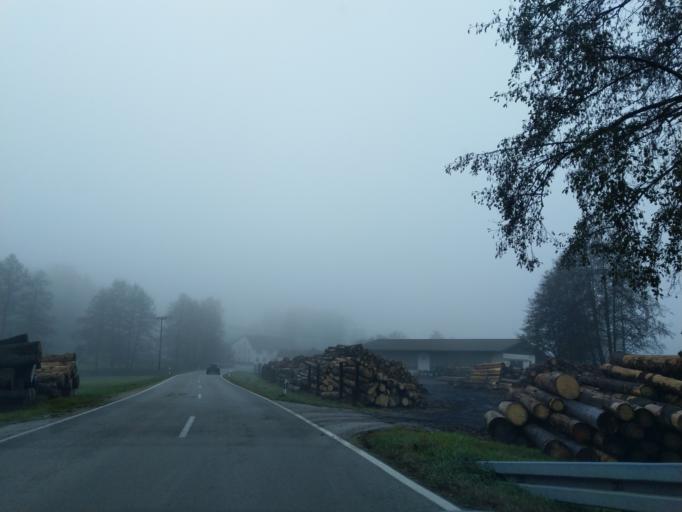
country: DE
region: Bavaria
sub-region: Lower Bavaria
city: Auerbach
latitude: 48.7738
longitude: 13.0935
